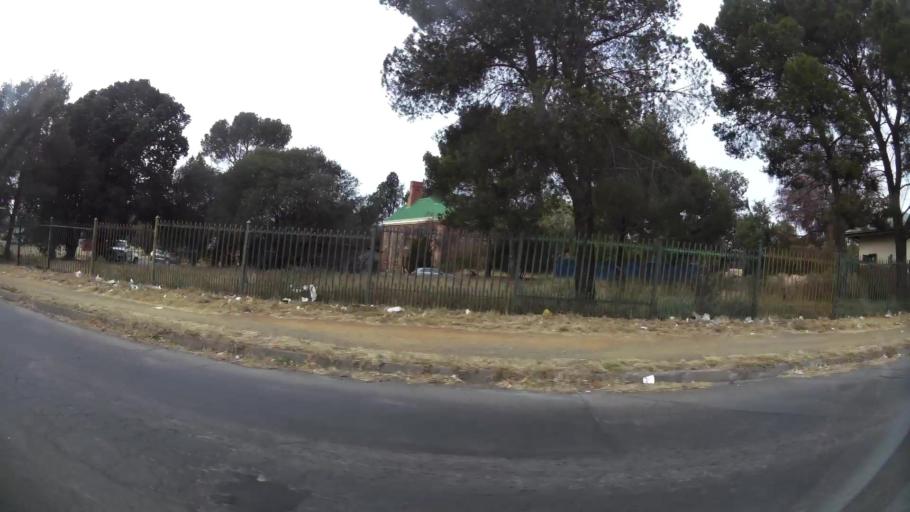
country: ZA
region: Orange Free State
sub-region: Mangaung Metropolitan Municipality
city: Bloemfontein
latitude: -29.1262
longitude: 26.2101
